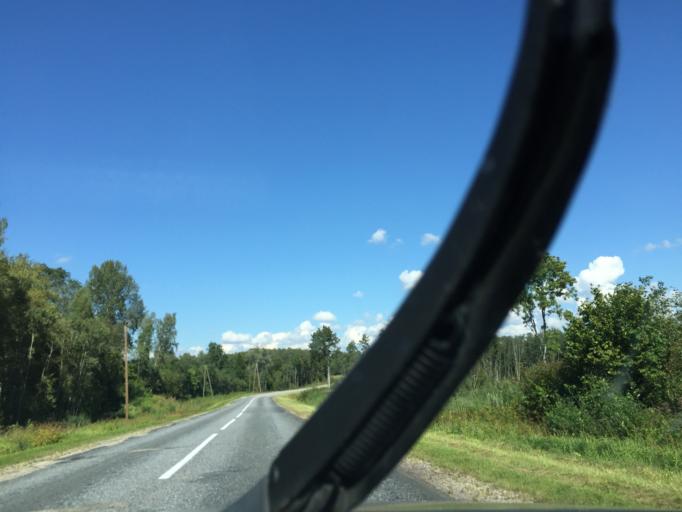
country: LV
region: Limbazu Rajons
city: Limbazi
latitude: 57.4381
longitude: 24.7185
